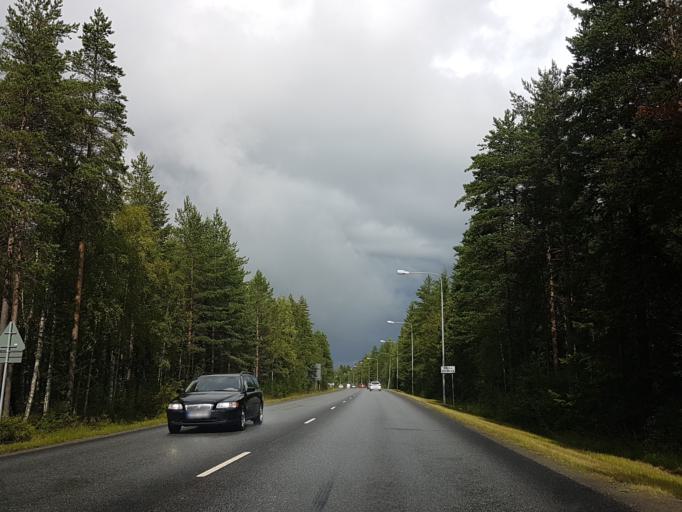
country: SE
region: Vaesterbotten
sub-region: Umea Kommun
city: Ersmark
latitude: 63.8487
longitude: 20.3424
